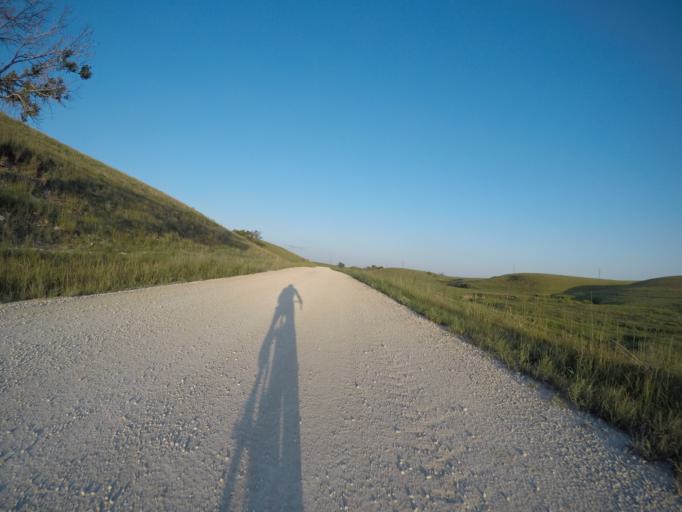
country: US
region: Kansas
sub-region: Riley County
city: Ogden
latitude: 39.0111
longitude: -96.6473
